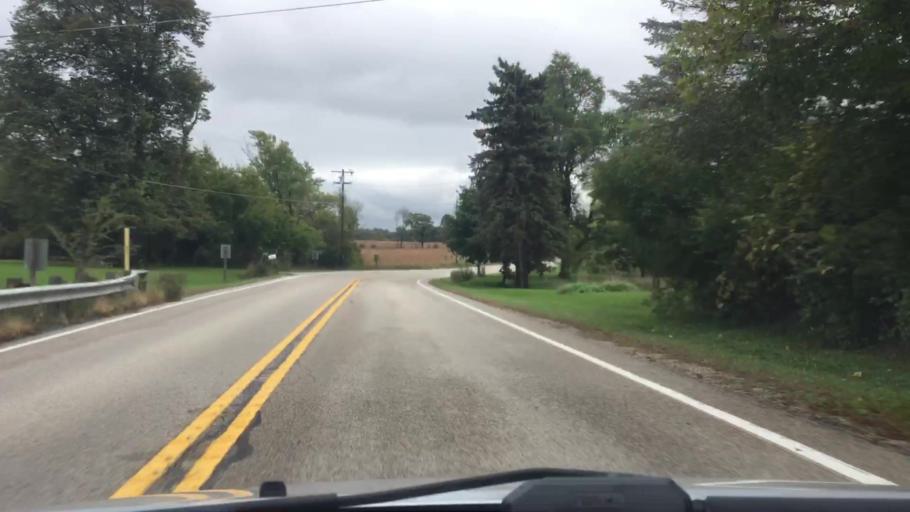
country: US
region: Wisconsin
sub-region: Waukesha County
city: Eagle
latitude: 42.8948
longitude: -88.4741
